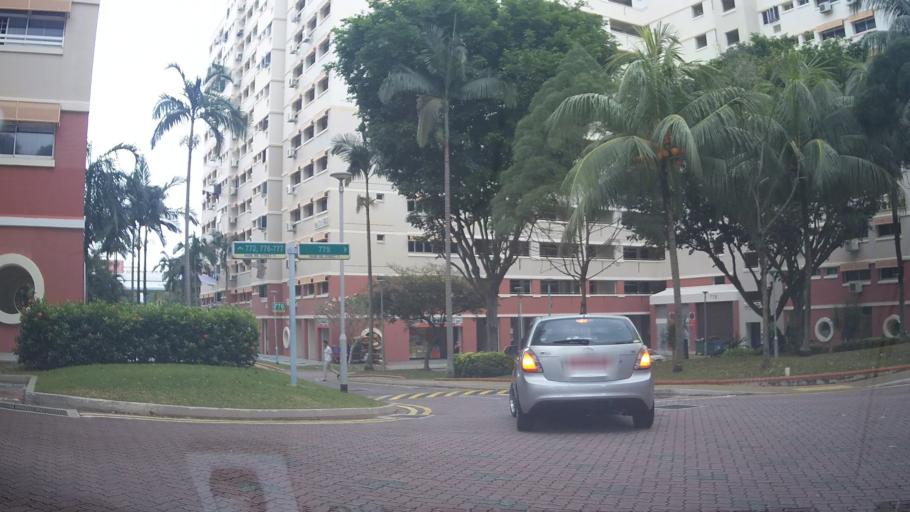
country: MY
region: Johor
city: Kampung Pasir Gudang Baru
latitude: 1.3746
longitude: 103.9365
